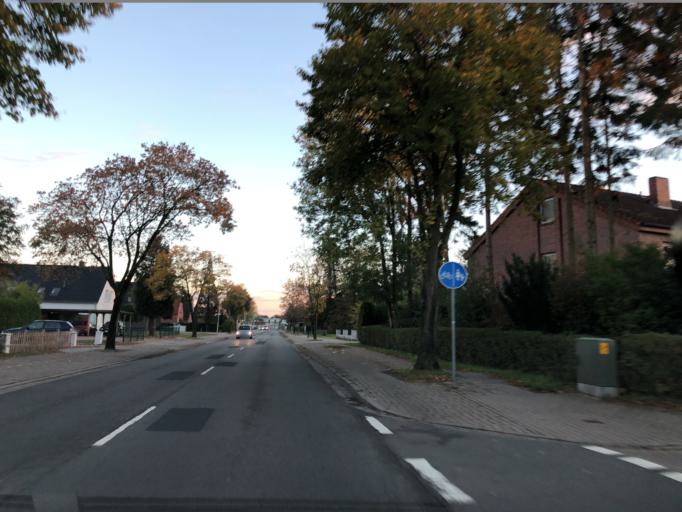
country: DE
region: Lower Saxony
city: Papenburg
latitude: 53.0846
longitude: 7.4099
